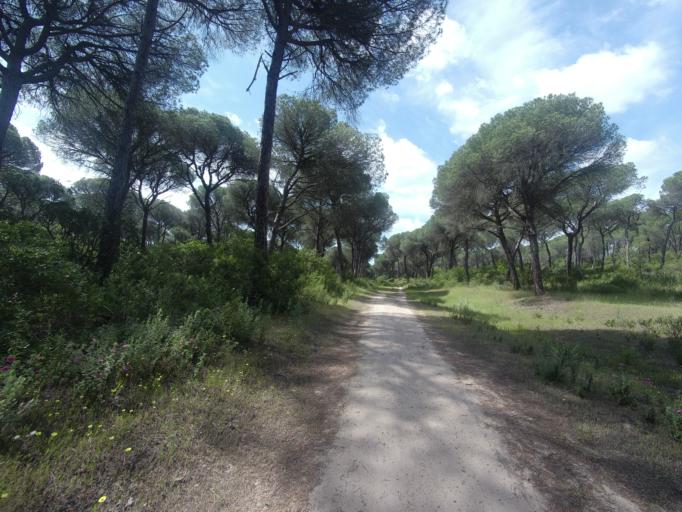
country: ES
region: Andalusia
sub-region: Provincia de Huelva
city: Aljaraque
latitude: 37.2268
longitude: -7.0677
